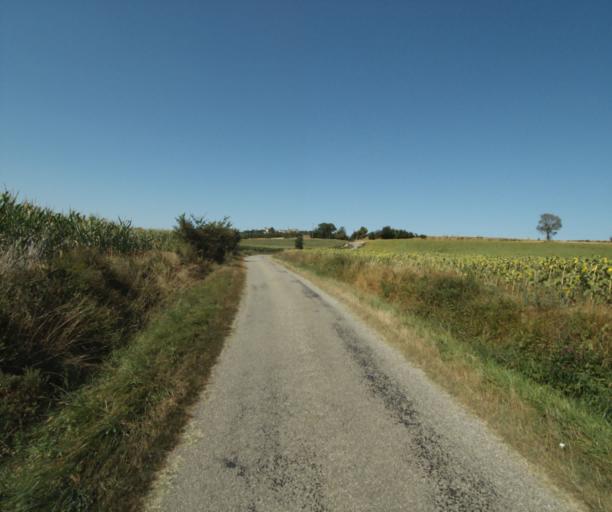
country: FR
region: Midi-Pyrenees
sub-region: Departement de la Haute-Garonne
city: Saint-Felix-Lauragais
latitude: 43.4785
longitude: 1.8955
